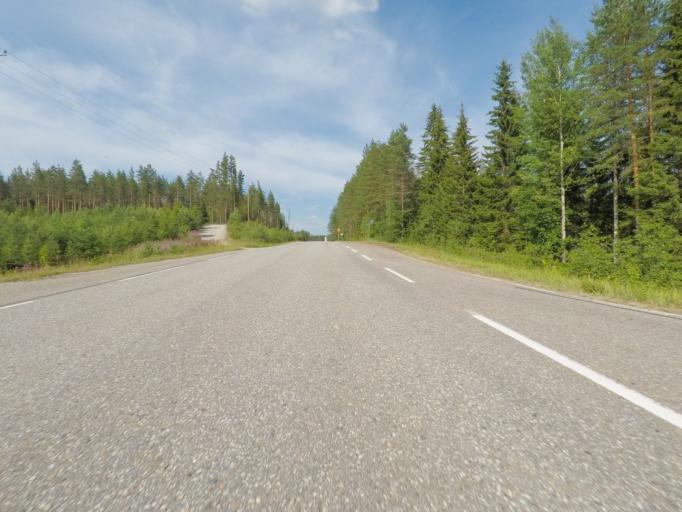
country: FI
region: Southern Savonia
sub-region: Savonlinna
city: Sulkava
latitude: 61.7833
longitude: 28.2404
